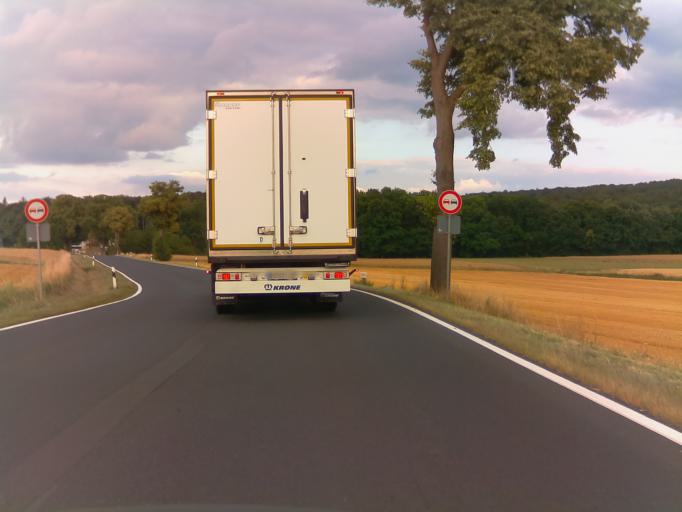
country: DE
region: Hesse
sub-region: Regierungsbezirk Giessen
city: Alsfeld
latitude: 50.7475
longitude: 9.3097
